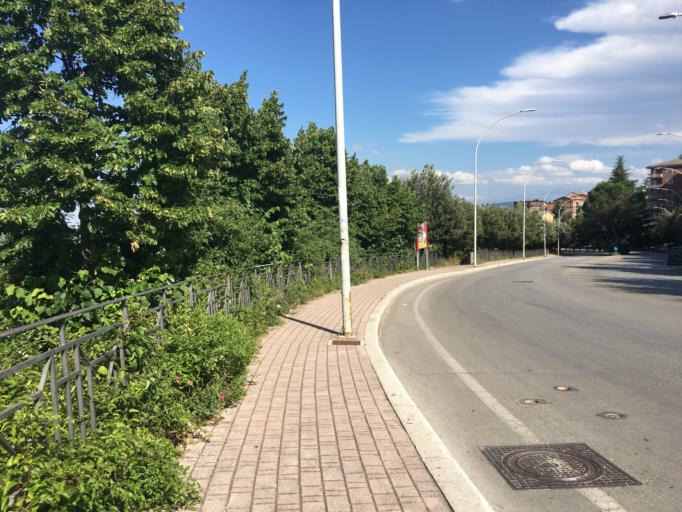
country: IT
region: Molise
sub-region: Provincia di Campobasso
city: Campobasso
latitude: 41.5546
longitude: 14.6613
